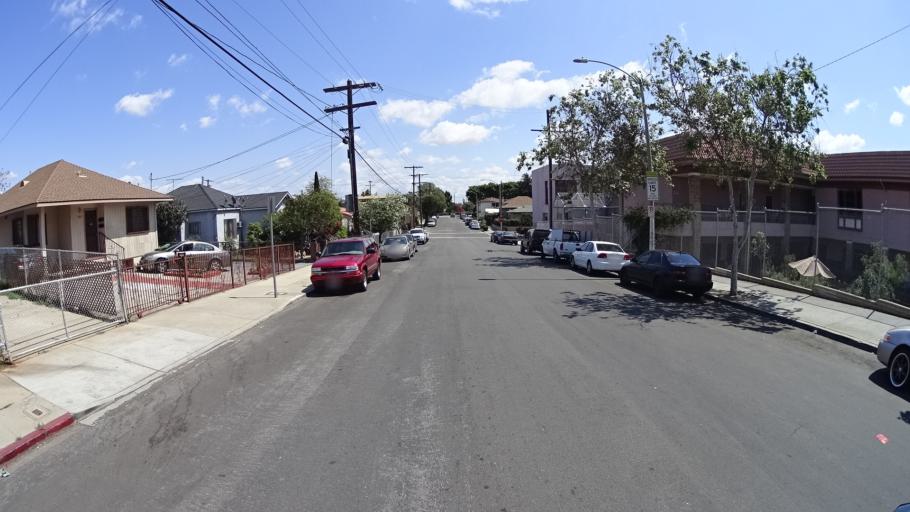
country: US
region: California
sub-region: Los Angeles County
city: Boyle Heights
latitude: 34.0507
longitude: -118.2076
